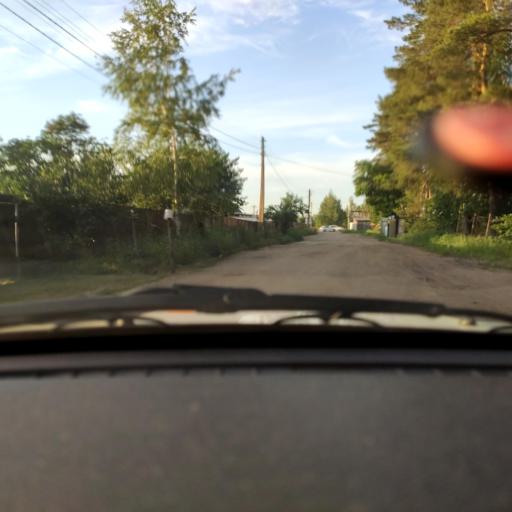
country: RU
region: Voronezj
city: Podgornoye
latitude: 51.8364
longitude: 39.1994
